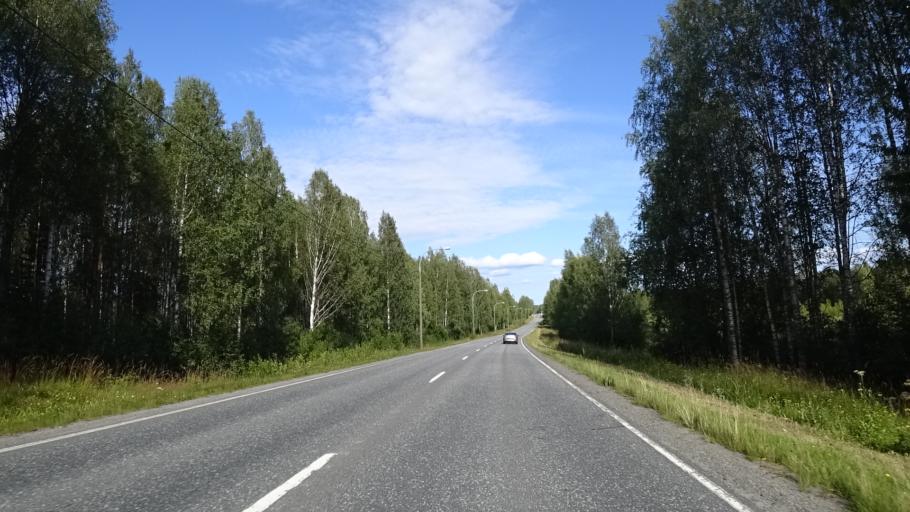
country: FI
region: North Karelia
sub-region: Joensuu
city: Eno
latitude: 62.7960
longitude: 30.0946
